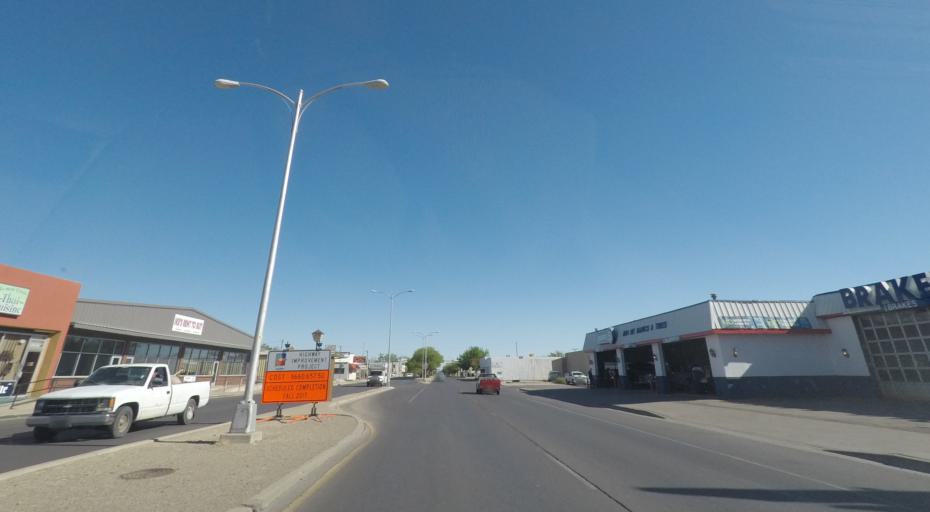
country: US
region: New Mexico
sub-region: Chaves County
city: Roswell
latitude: 33.3871
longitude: -104.5227
